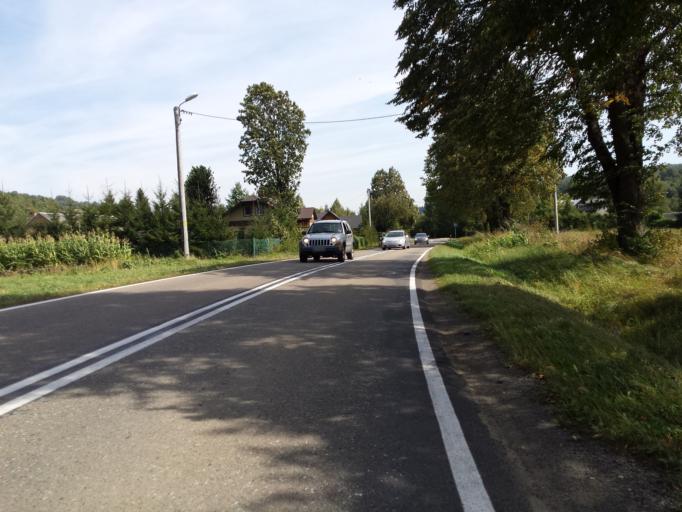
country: PL
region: Subcarpathian Voivodeship
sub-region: Powiat leski
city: Baligrod
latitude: 49.3982
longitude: 22.2808
